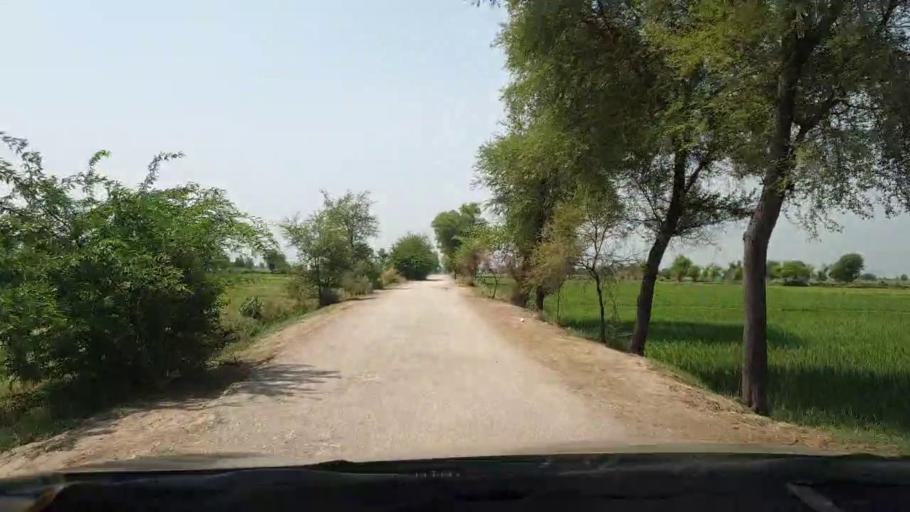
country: PK
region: Sindh
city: Naudero
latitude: 27.6433
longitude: 68.2747
